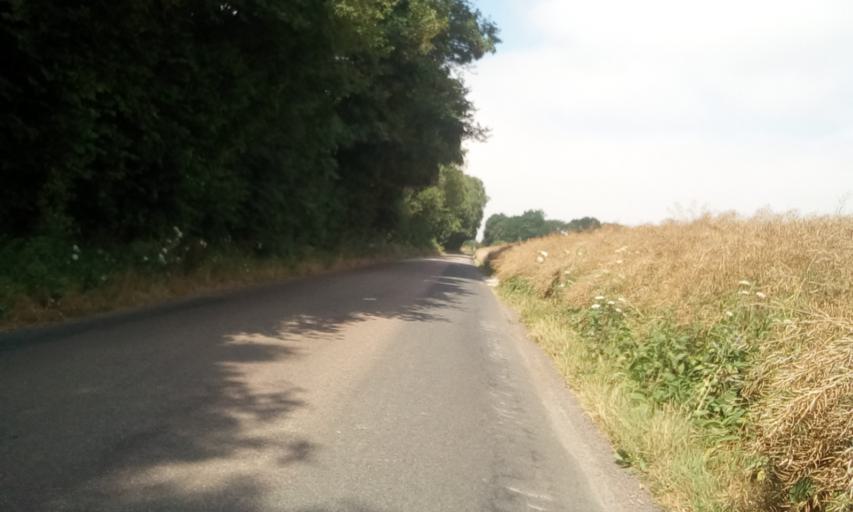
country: FR
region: Lower Normandy
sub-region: Departement du Calvados
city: Douvres-la-Delivrande
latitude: 49.2920
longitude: -0.4117
